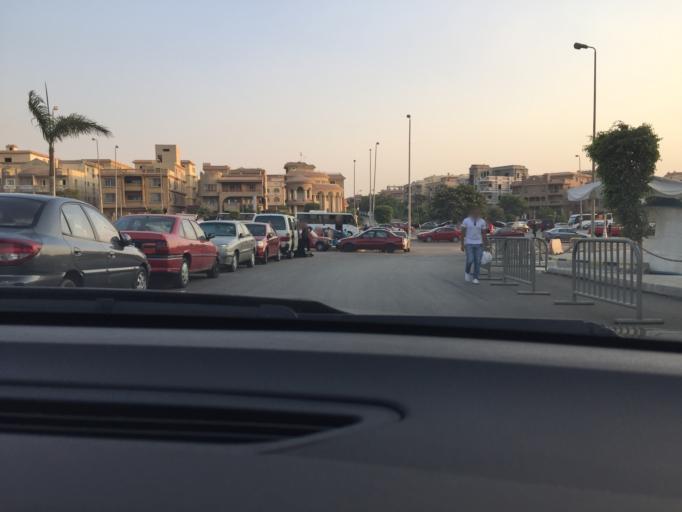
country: EG
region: Muhafazat al Qahirah
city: Cairo
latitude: 30.0171
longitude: 31.4257
